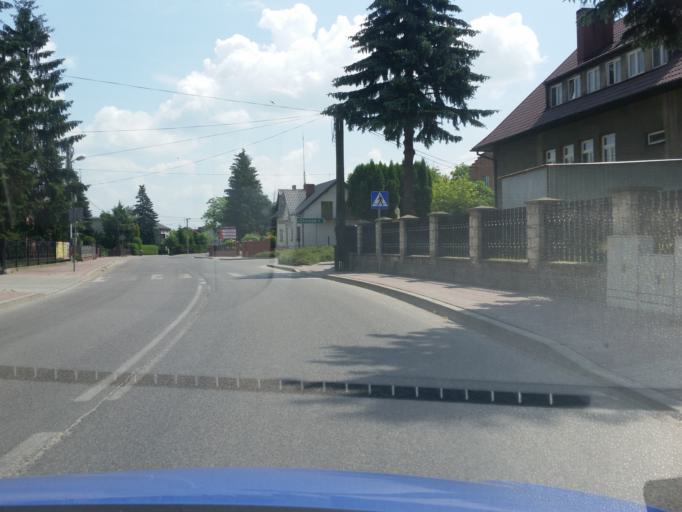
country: PL
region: Swietokrzyskie
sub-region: Powiat kazimierski
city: Skalbmierz
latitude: 50.3172
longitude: 20.3993
